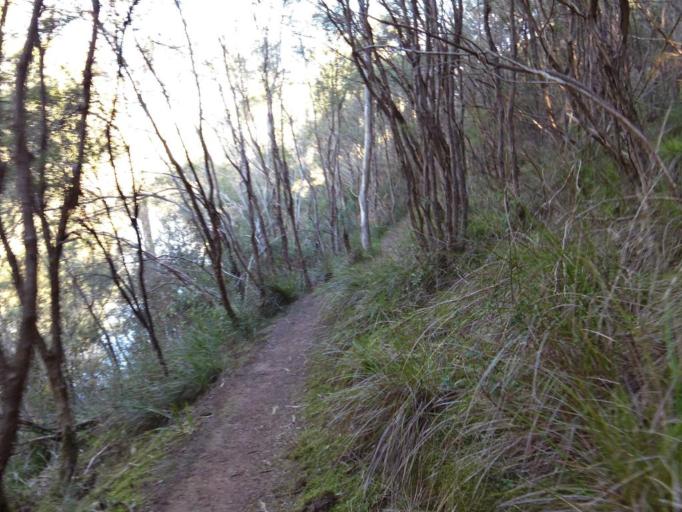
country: AU
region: Victoria
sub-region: Manningham
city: Warrandyte
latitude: -37.7342
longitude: 145.2385
